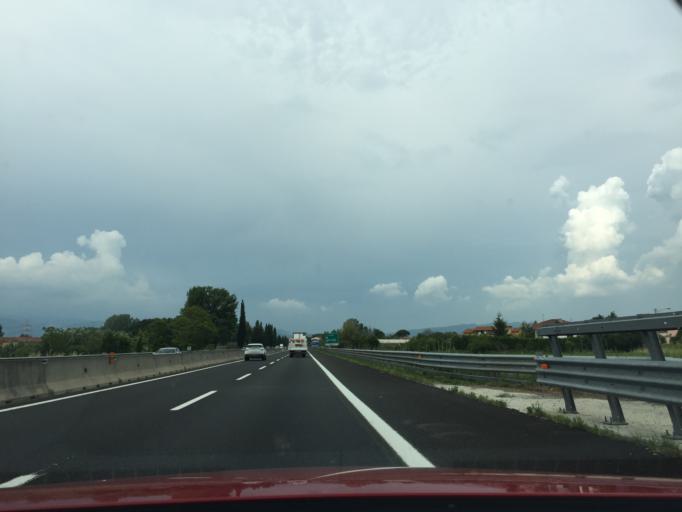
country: IT
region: Tuscany
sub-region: Provincia di Pistoia
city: Chiesina Uzzanese
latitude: 43.8352
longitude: 10.7078
